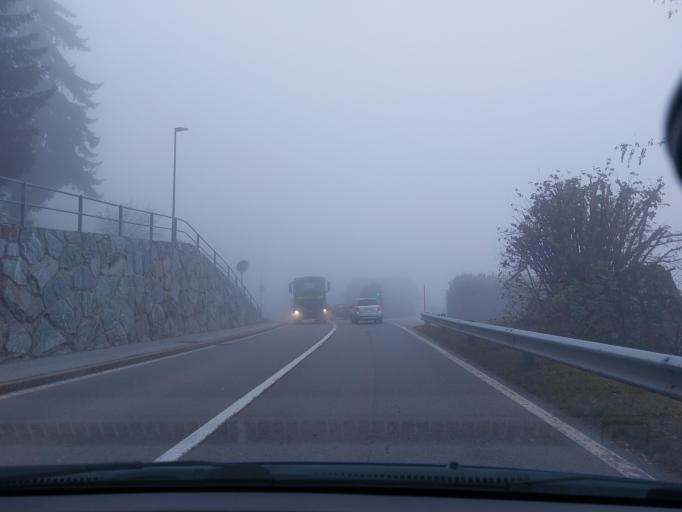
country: CH
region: Valais
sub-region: Sierre District
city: Randogne
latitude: 46.3100
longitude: 7.5058
